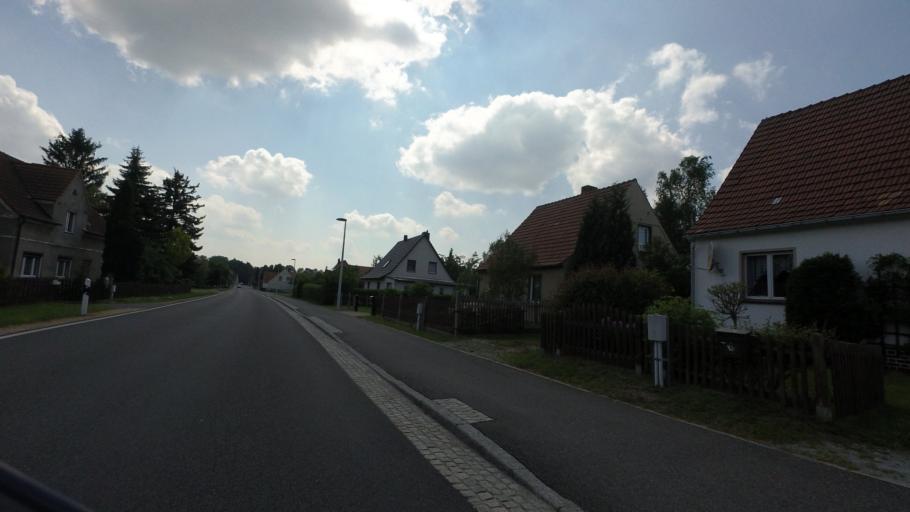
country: DE
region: Saxony
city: Mucka
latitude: 51.3006
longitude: 14.6674
